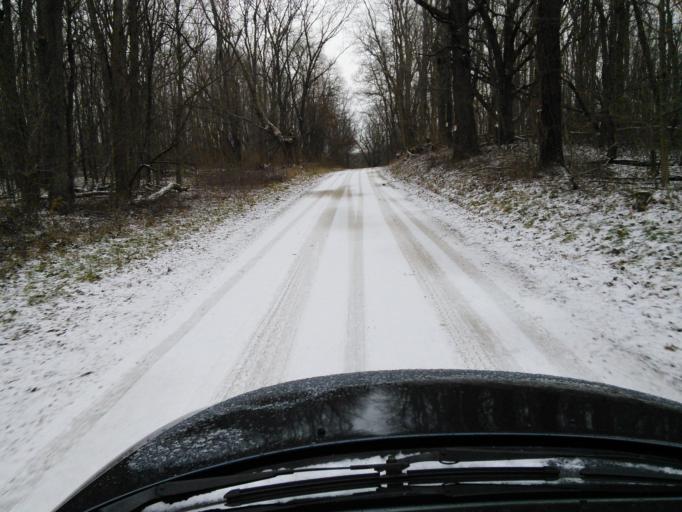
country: US
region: Michigan
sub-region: Jackson County
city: Grass Lake
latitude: 42.3107
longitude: -84.1895
